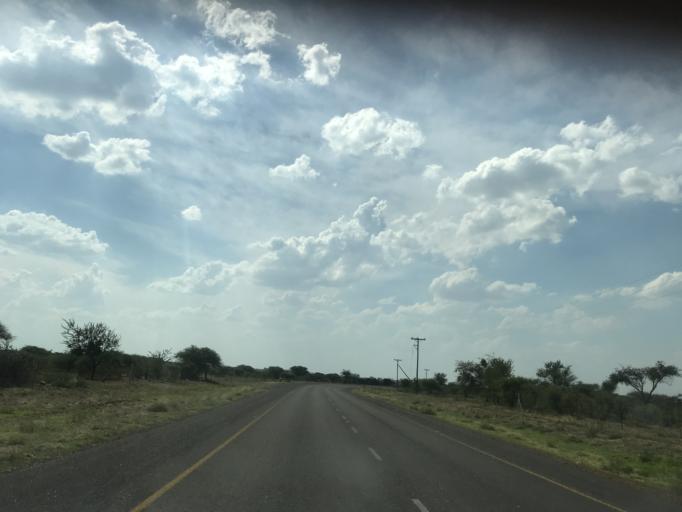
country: BW
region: South East
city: Janeng
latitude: -25.4919
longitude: 25.6291
